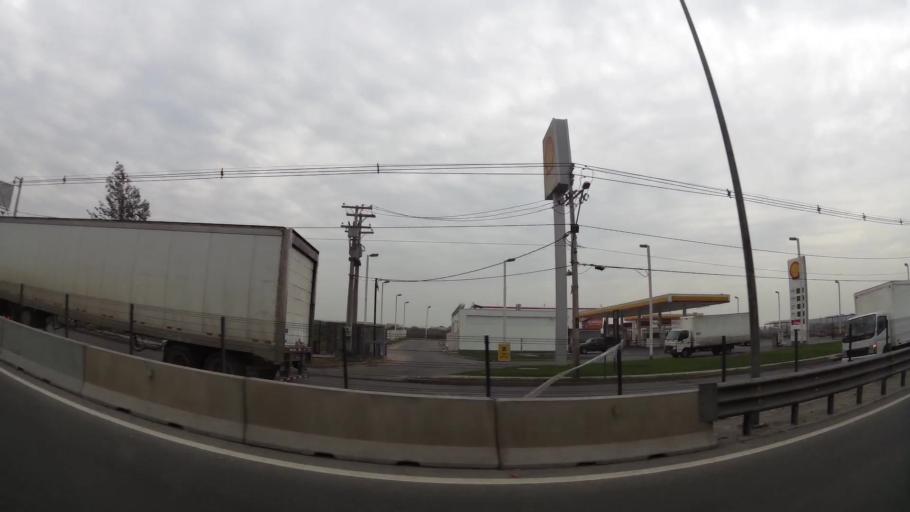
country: CL
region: Santiago Metropolitan
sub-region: Provincia de Maipo
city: San Bernardo
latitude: -33.5179
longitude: -70.7098
